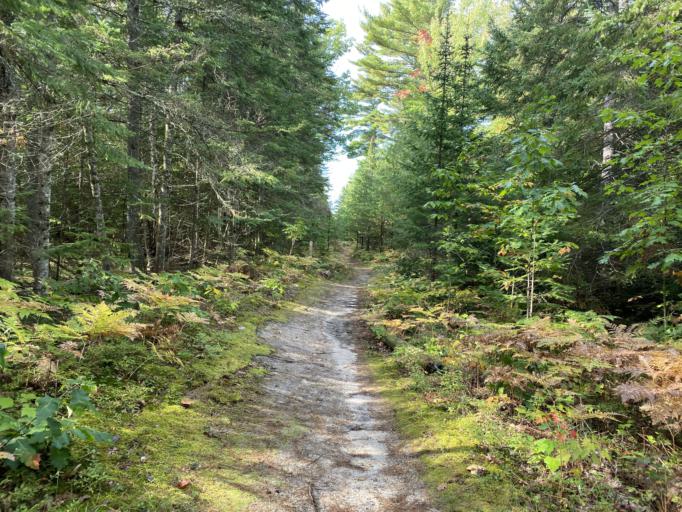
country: US
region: Michigan
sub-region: Mackinac County
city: Saint Ignace
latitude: 45.7465
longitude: -84.8908
